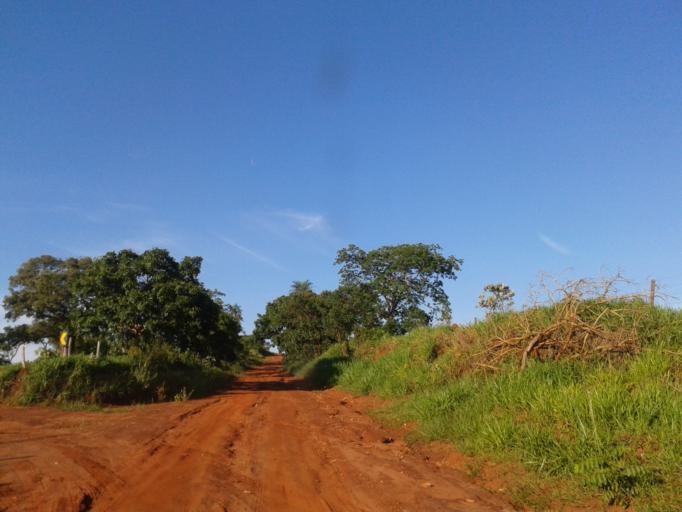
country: BR
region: Minas Gerais
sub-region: Santa Vitoria
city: Santa Vitoria
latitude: -18.9652
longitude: -49.8749
